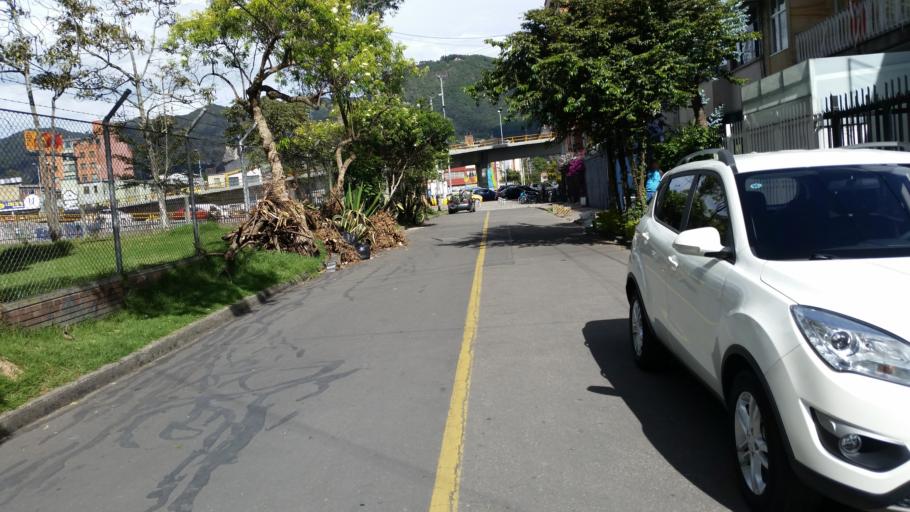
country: CO
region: Bogota D.C.
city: Bogota
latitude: 4.6334
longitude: -74.0806
